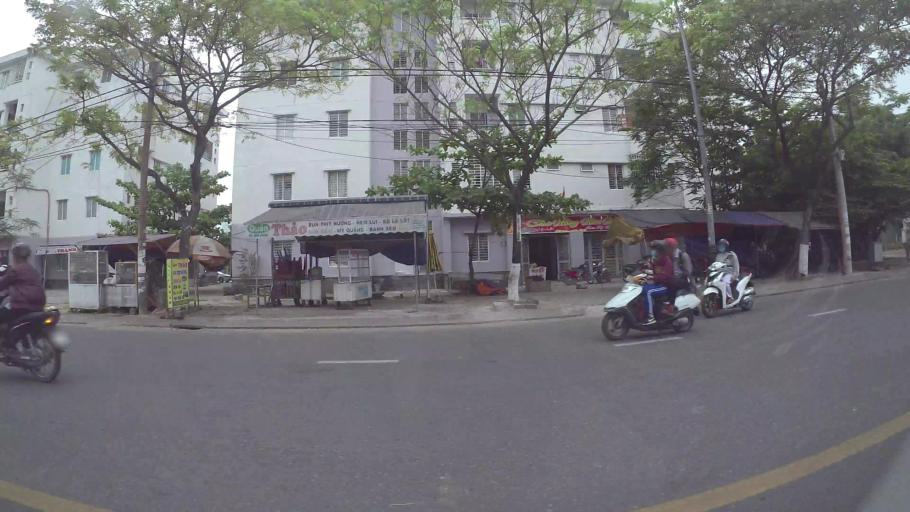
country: VN
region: Da Nang
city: Lien Chieu
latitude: 16.0754
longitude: 108.1685
